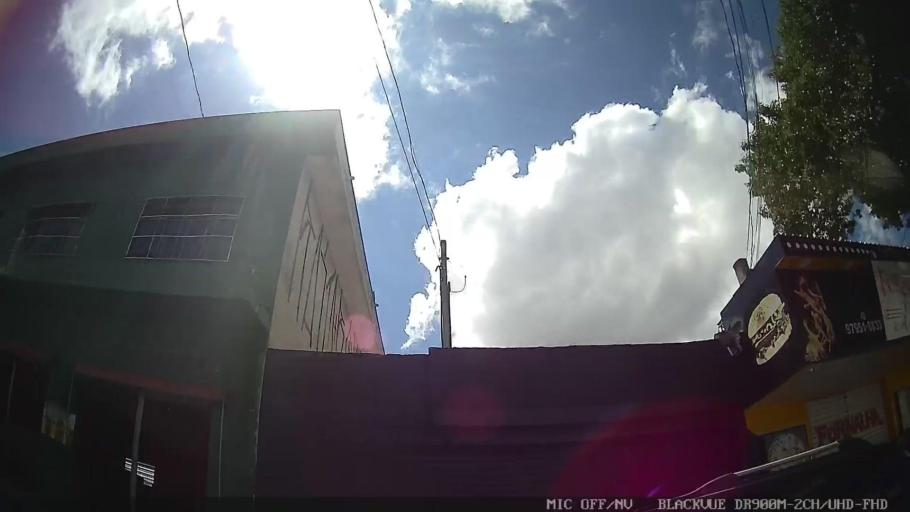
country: BR
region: Sao Paulo
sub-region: Diadema
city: Diadema
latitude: -23.6675
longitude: -46.6054
